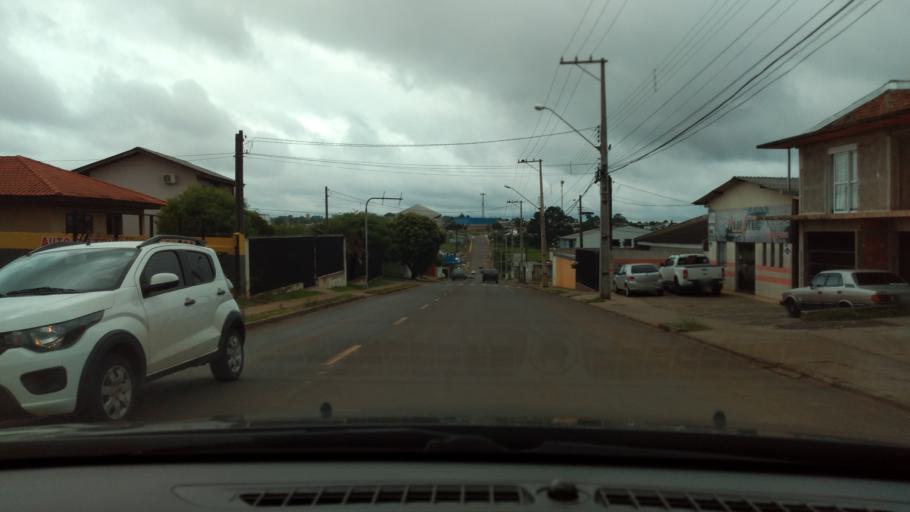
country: BR
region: Parana
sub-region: Guarapuava
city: Guarapuava
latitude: -25.3936
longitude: -51.4927
